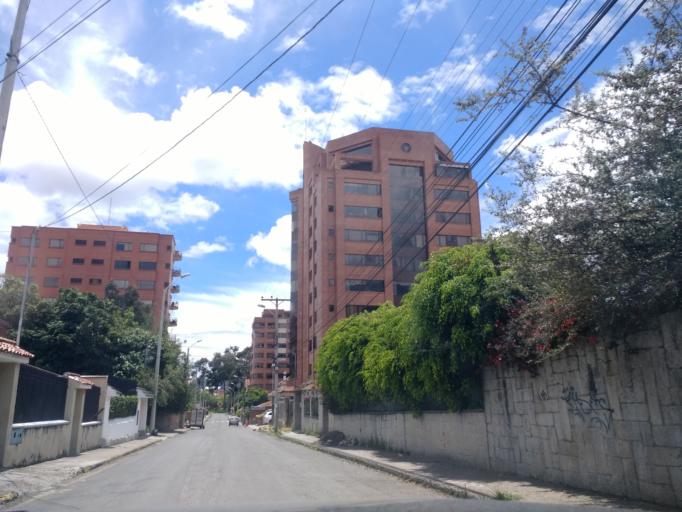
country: EC
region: Azuay
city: Cuenca
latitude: -2.8910
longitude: -79.0259
